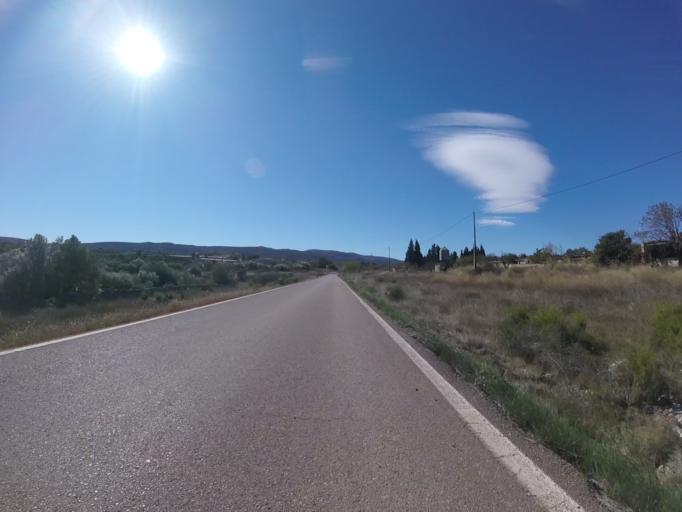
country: ES
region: Valencia
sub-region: Provincia de Castello
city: Albocasser
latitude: 40.3723
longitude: 0.0195
